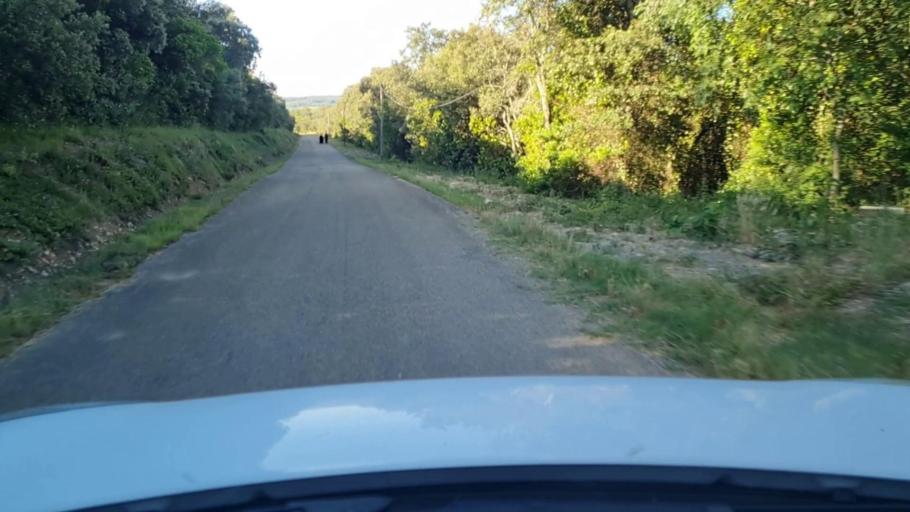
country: FR
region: Languedoc-Roussillon
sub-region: Departement du Gard
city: Villevieille
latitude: 43.8517
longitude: 4.0794
